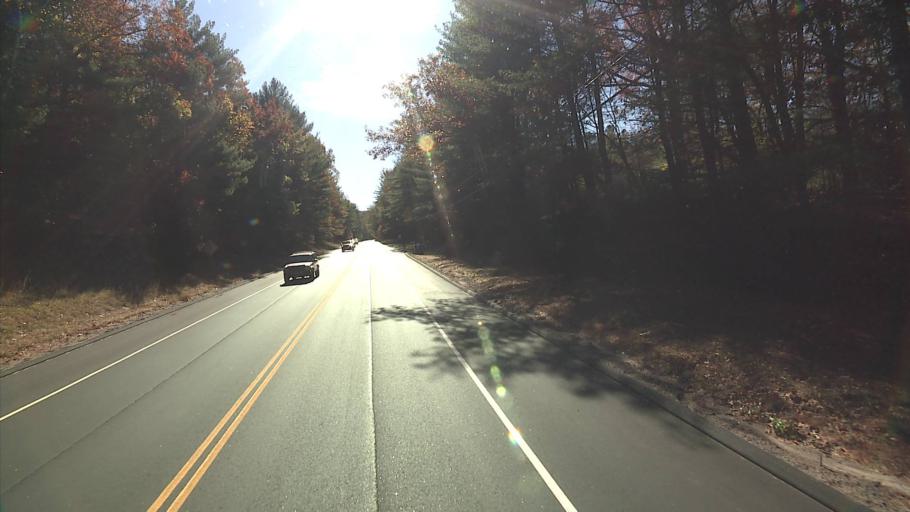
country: US
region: Connecticut
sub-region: Litchfield County
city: Thomaston
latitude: 41.6493
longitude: -73.0956
